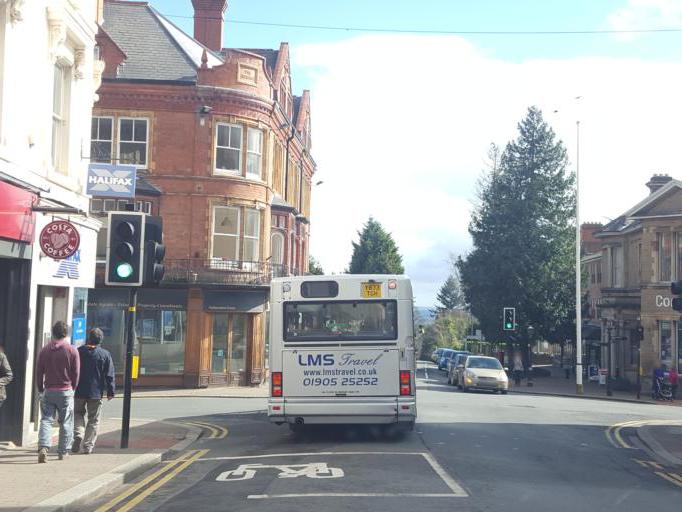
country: GB
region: England
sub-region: Worcestershire
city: Great Malvern
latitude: 52.1115
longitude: -2.3273
